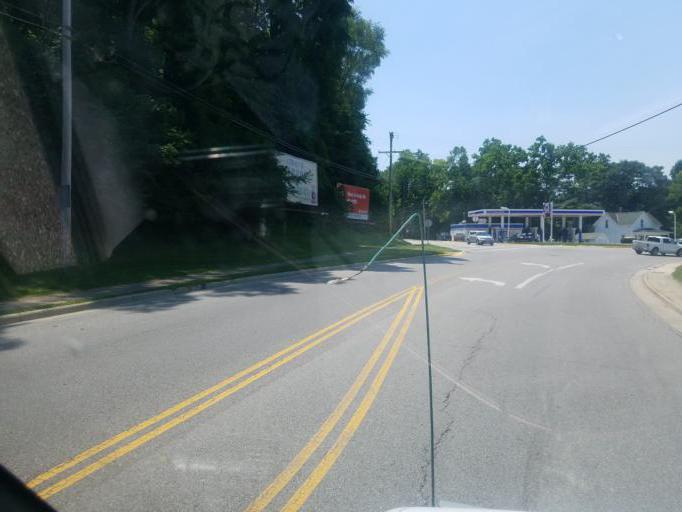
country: US
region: Ohio
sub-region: Shelby County
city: Sidney
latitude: 40.2874
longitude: -84.1477
